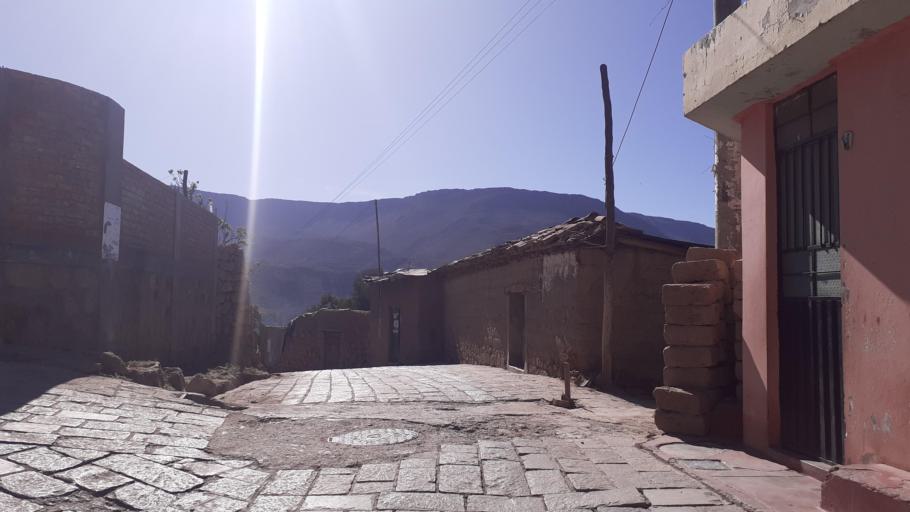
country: PE
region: Arequipa
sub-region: Provincia de Condesuyos
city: Chuquibamba
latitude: -15.8353
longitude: -72.6533
